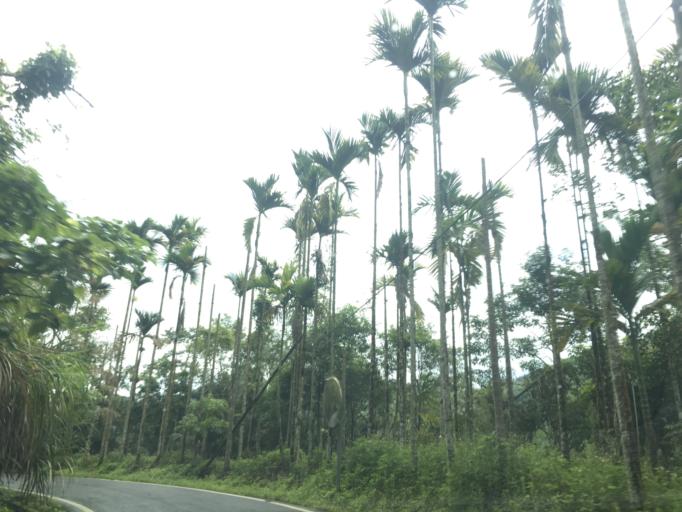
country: TW
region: Taiwan
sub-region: Yunlin
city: Douliu
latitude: 23.5652
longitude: 120.6461
